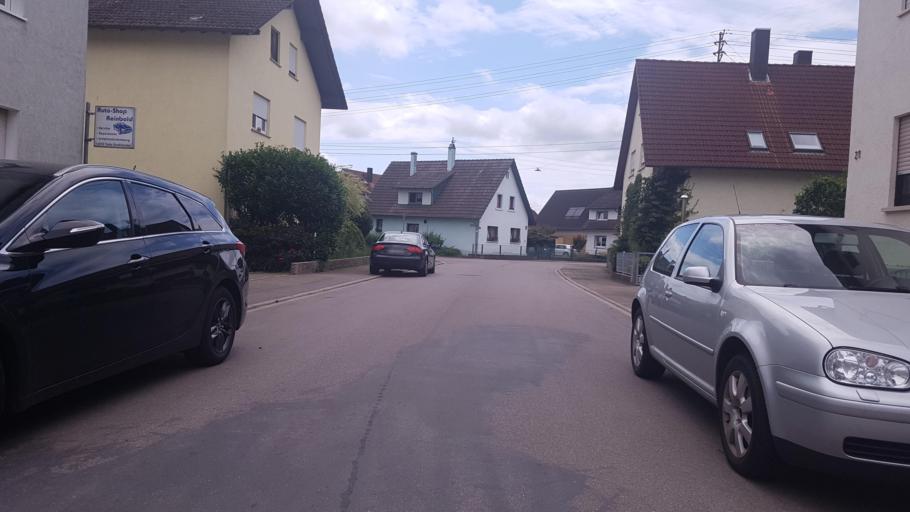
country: DE
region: Baden-Wuerttemberg
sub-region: Karlsruhe Region
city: Iffezheim
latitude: 48.8453
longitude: 8.1385
